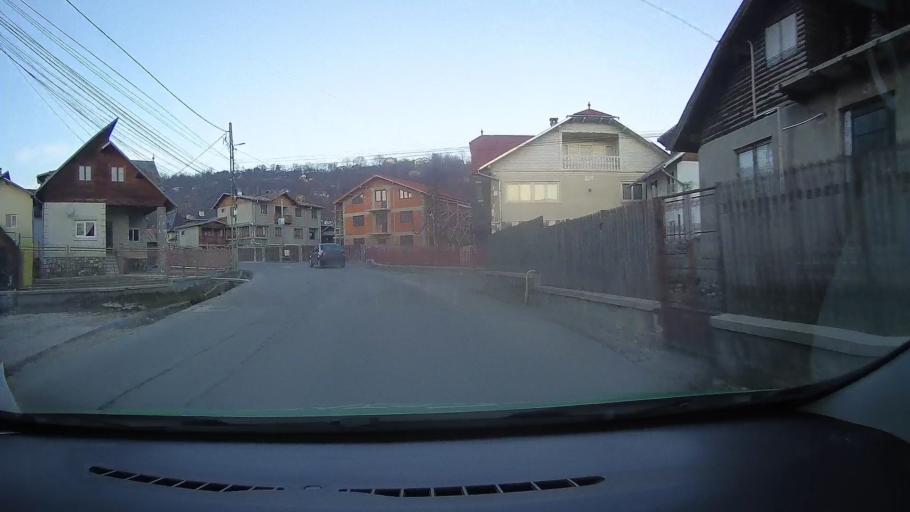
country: RO
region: Prahova
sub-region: Comuna Comarnic
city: Comarnic
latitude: 45.2472
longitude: 25.6367
